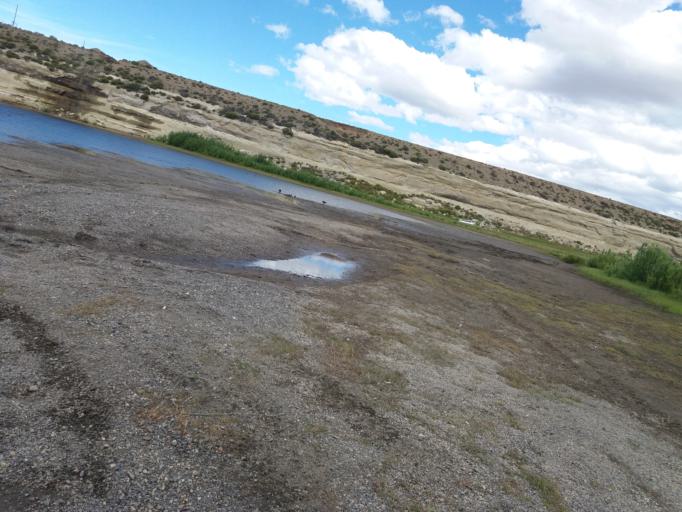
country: AR
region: Santa Cruz
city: Rio Gallegos
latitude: -51.6645
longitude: -69.6420
